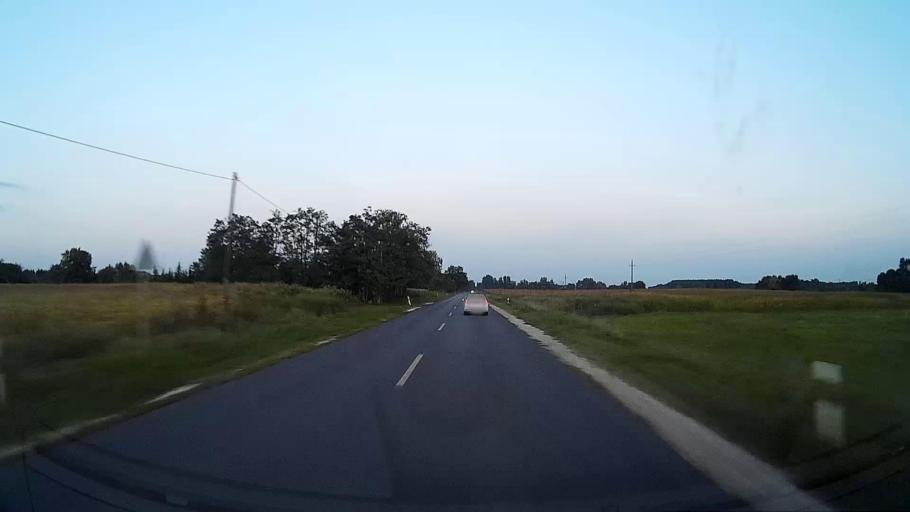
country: HU
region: Pest
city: Albertirsa
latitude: 47.2446
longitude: 19.6321
